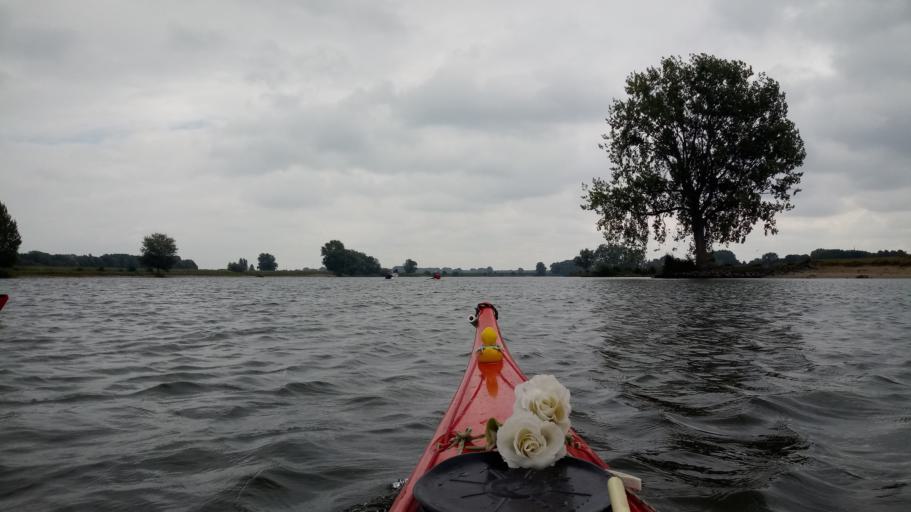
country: NL
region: Gelderland
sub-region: Gemeente Maasdriel
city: Hedel
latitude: 51.7427
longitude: 5.2241
